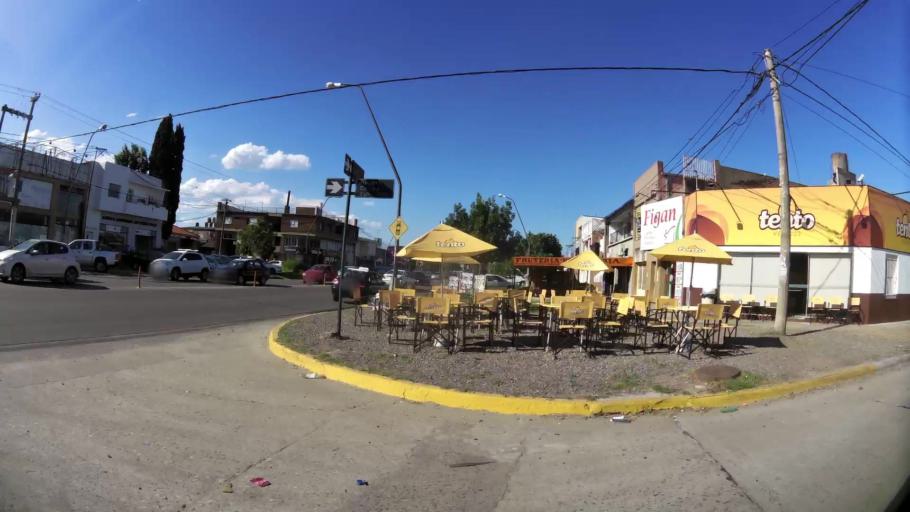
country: AR
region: Santa Fe
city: Santa Fe de la Vera Cruz
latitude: -31.6156
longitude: -60.6970
